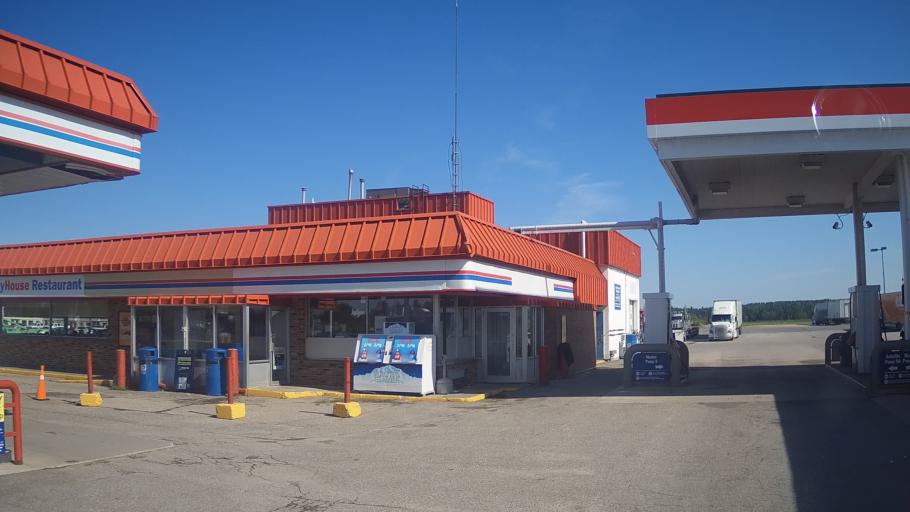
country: CA
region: Ontario
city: Dryden
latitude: 49.7867
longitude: -92.8323
